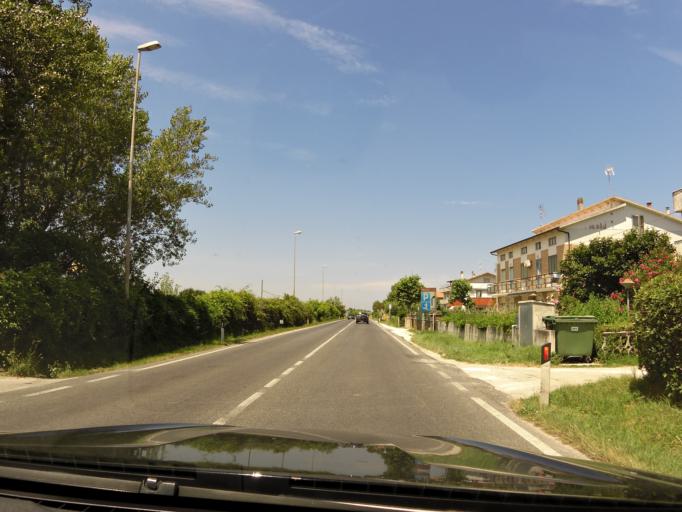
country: IT
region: The Marches
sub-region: Provincia di Pesaro e Urbino
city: Marotta
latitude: 43.7909
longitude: 13.1045
